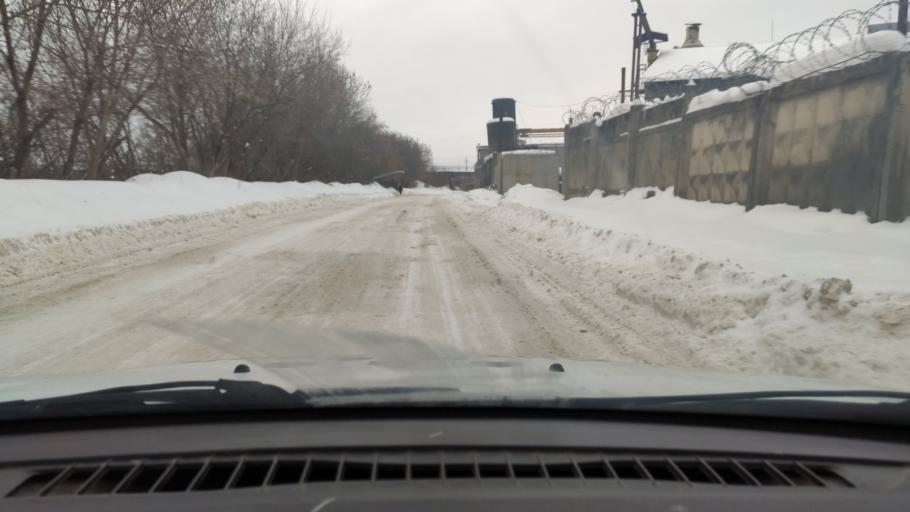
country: RU
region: Perm
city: Kungur
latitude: 57.4471
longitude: 56.9229
